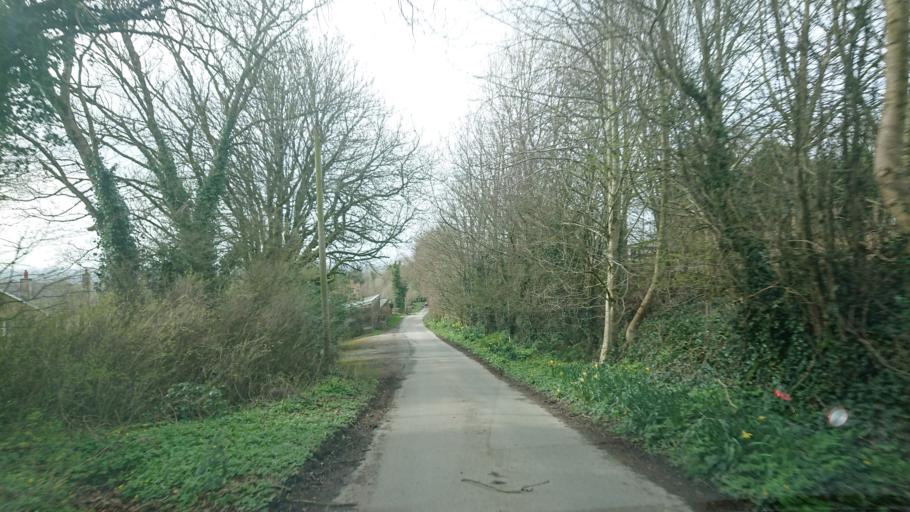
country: IE
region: Leinster
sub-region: Kildare
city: Eadestown
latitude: 53.1597
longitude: -6.5883
